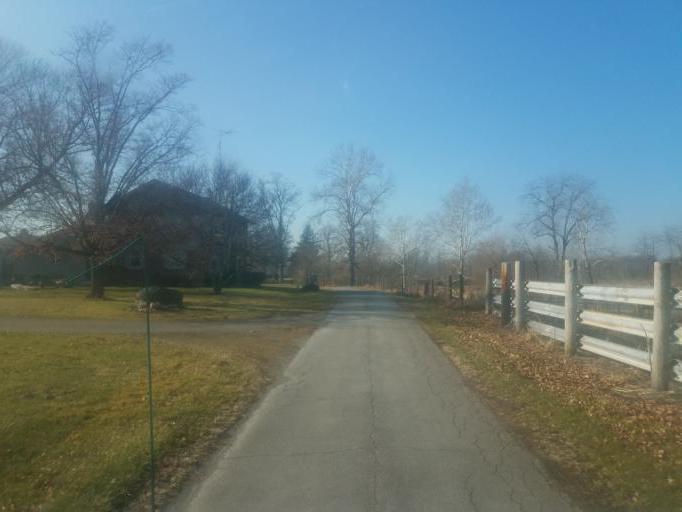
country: US
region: Ohio
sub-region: Seneca County
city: Tiffin
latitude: 41.0616
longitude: -83.0299
